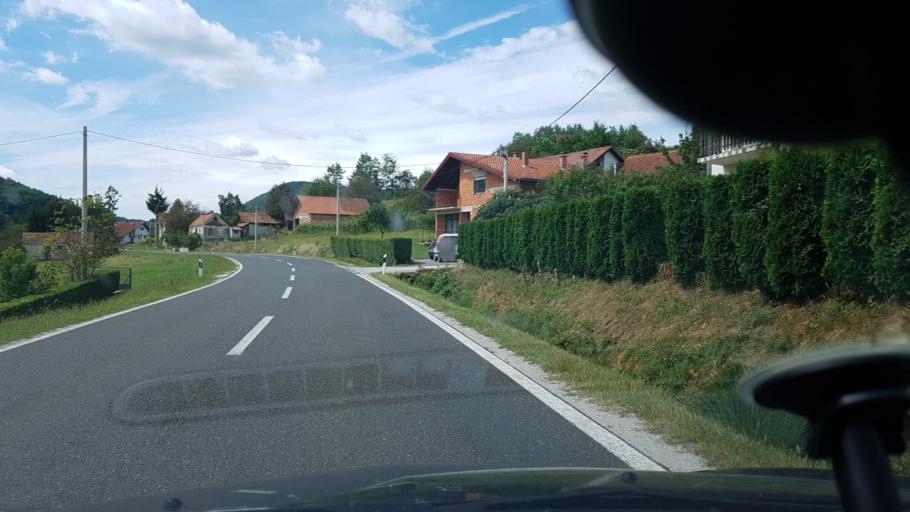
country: HR
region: Varazdinska
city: Lepoglava
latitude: 46.2131
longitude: 16.0166
